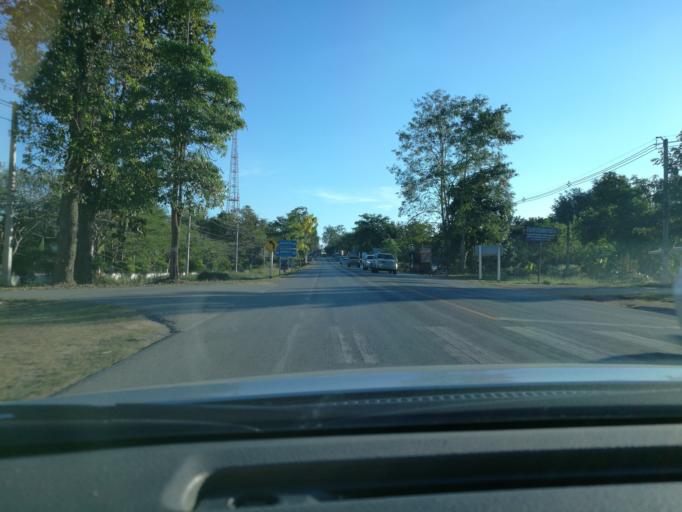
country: TH
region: Phitsanulok
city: Nakhon Thai
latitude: 17.0606
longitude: 100.8098
